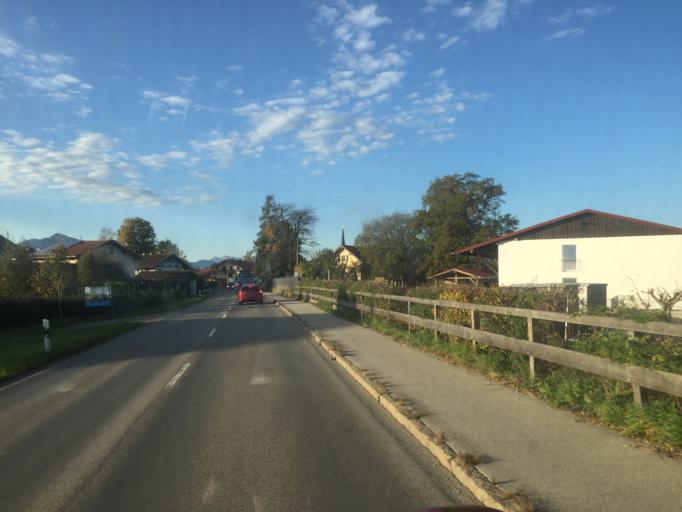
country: DE
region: Bavaria
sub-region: Upper Bavaria
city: Chieming
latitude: 47.8953
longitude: 12.5436
